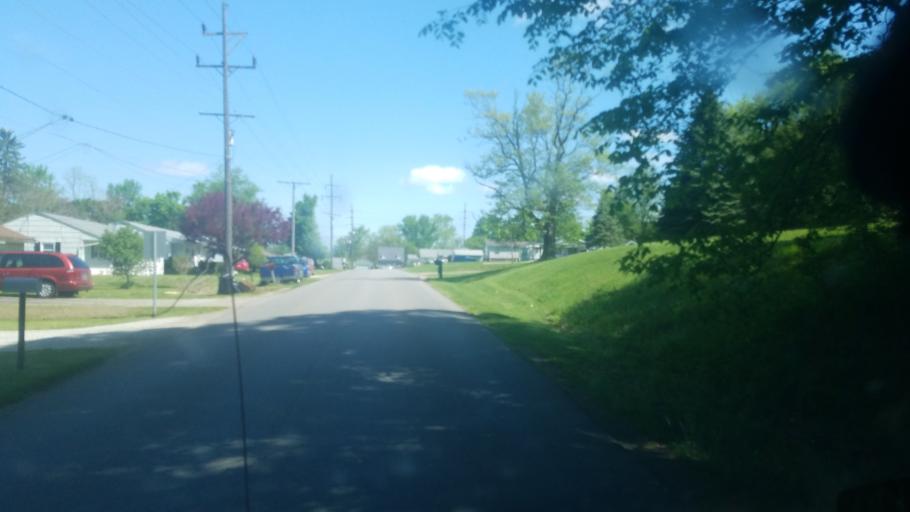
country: US
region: Ohio
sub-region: Richland County
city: Lincoln Heights
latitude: 40.7685
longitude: -82.4842
